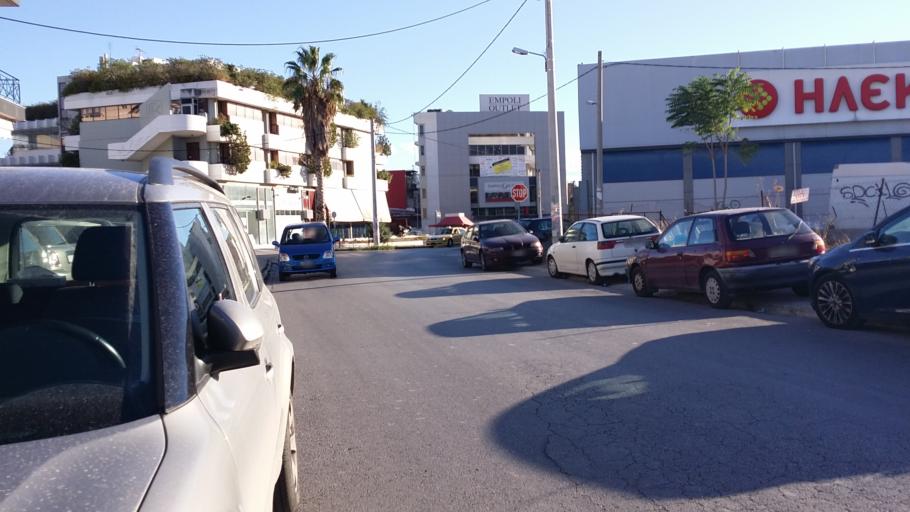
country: GR
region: Attica
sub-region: Nomarchia Athinas
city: Irakleio
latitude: 38.0512
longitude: 23.7520
